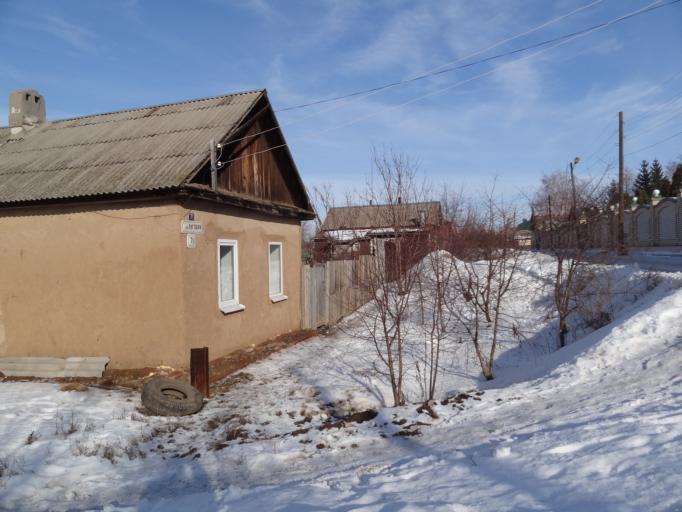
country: RU
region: Saratov
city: Engel's
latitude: 51.4774
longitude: 46.1121
